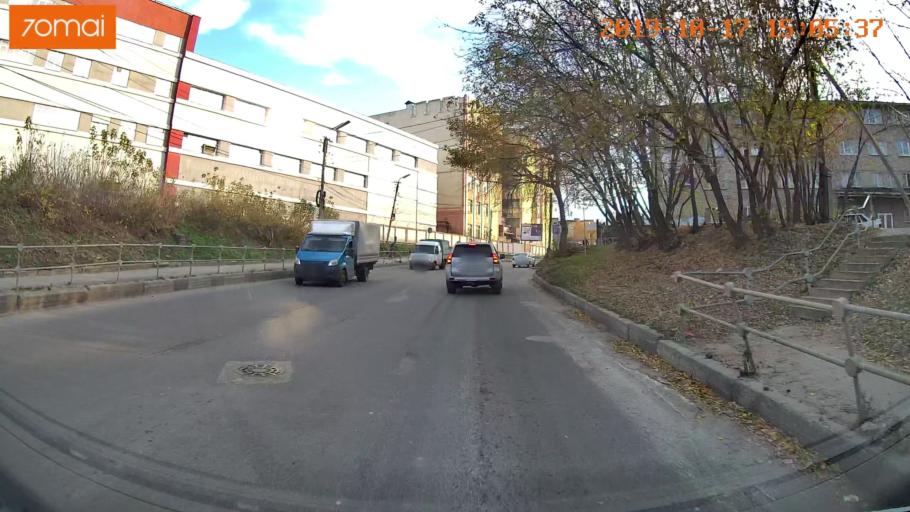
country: RU
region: Rjazan
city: Ryazan'
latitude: 54.6342
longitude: 39.7241
